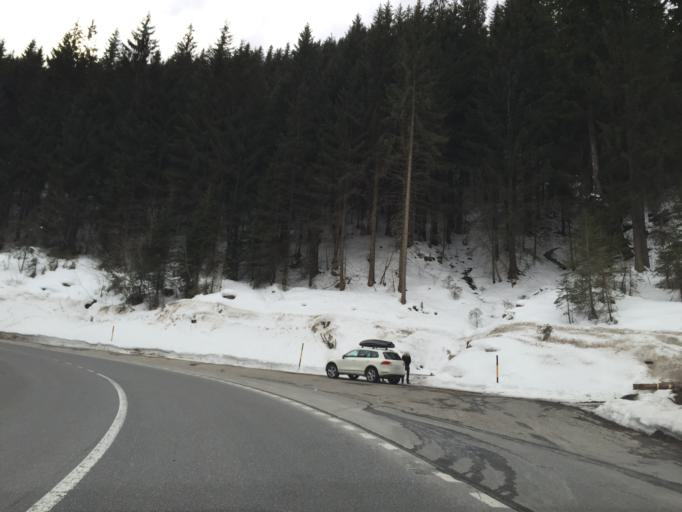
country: CH
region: Grisons
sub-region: Praettigau/Davos District
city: Klosters Serneus
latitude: 46.8546
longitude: 9.8783
